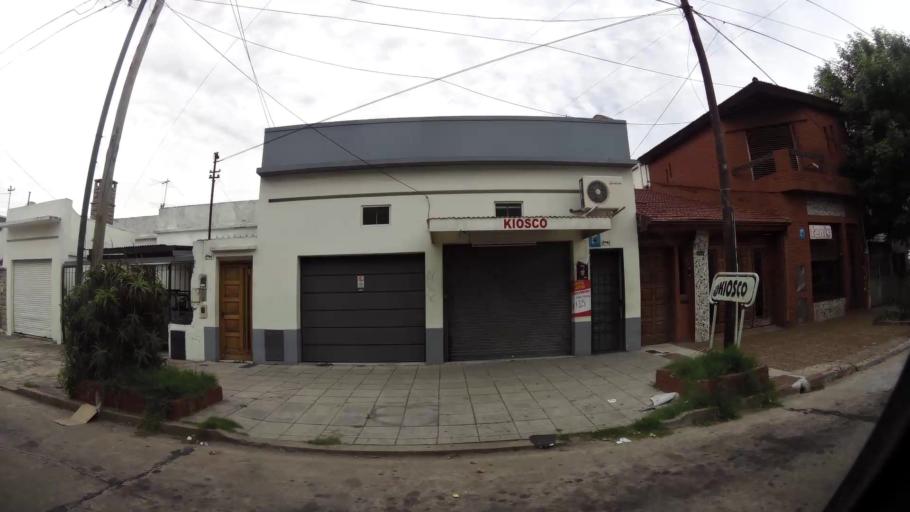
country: AR
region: Buenos Aires
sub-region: Partido de Lanus
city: Lanus
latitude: -34.6761
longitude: -58.3982
